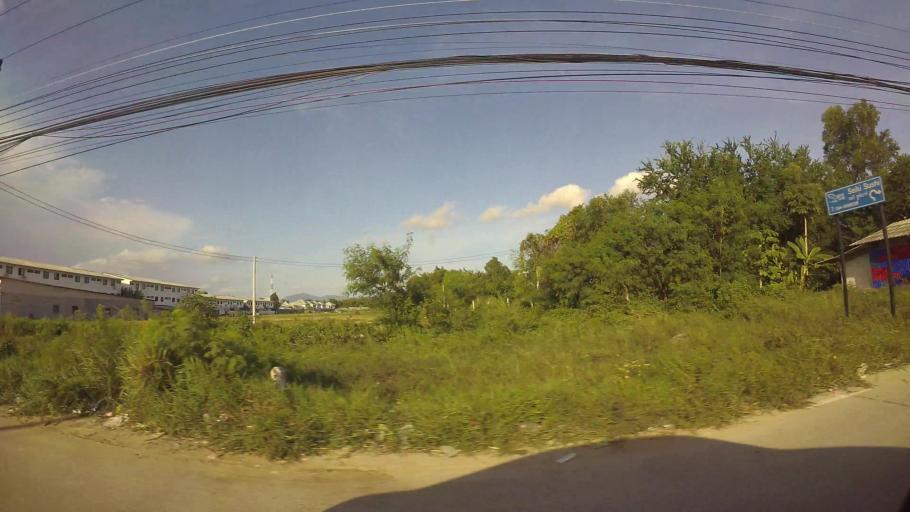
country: TH
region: Rayong
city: Rayong
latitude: 12.6883
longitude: 101.2858
